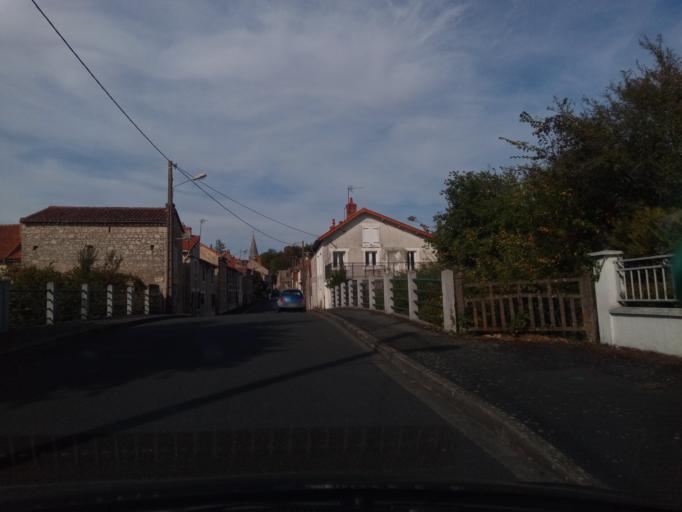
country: FR
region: Poitou-Charentes
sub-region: Departement de la Vienne
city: Montmorillon
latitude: 46.4195
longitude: 0.8627
